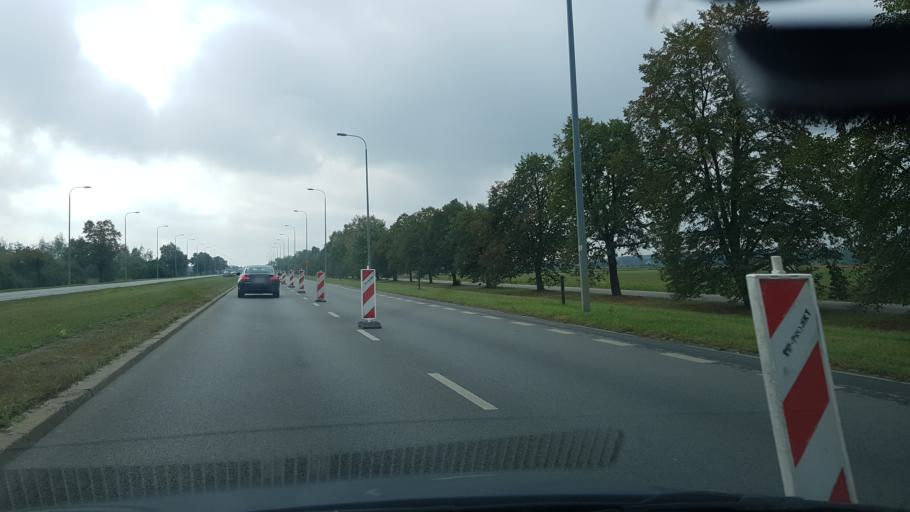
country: PL
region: Masovian Voivodeship
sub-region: Warszawa
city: Kabaty
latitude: 52.1432
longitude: 21.0959
